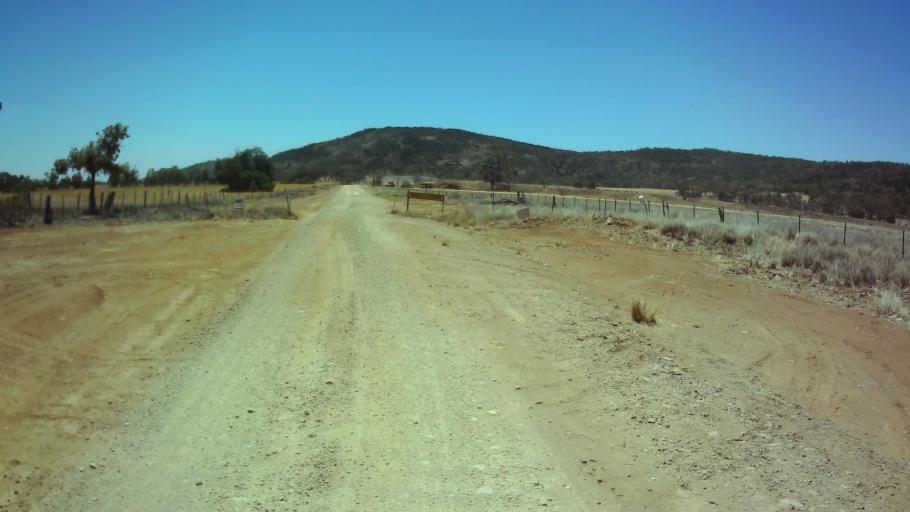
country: AU
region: New South Wales
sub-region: Weddin
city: Grenfell
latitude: -33.8592
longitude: 148.1071
